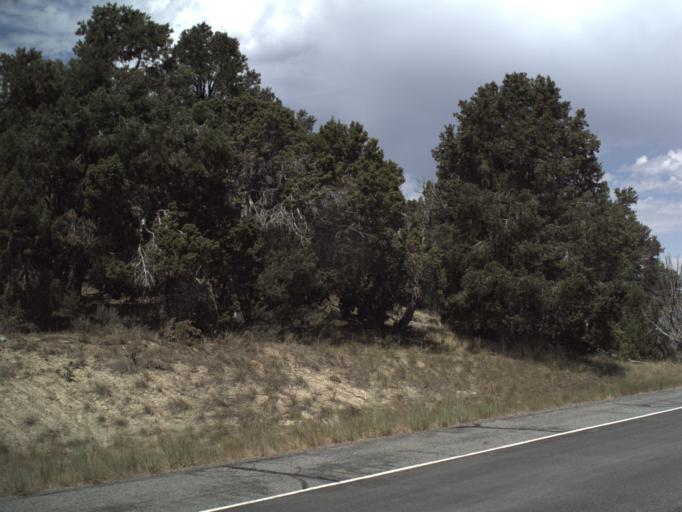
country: US
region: Utah
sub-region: Utah County
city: Genola
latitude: 39.9566
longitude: -112.2426
